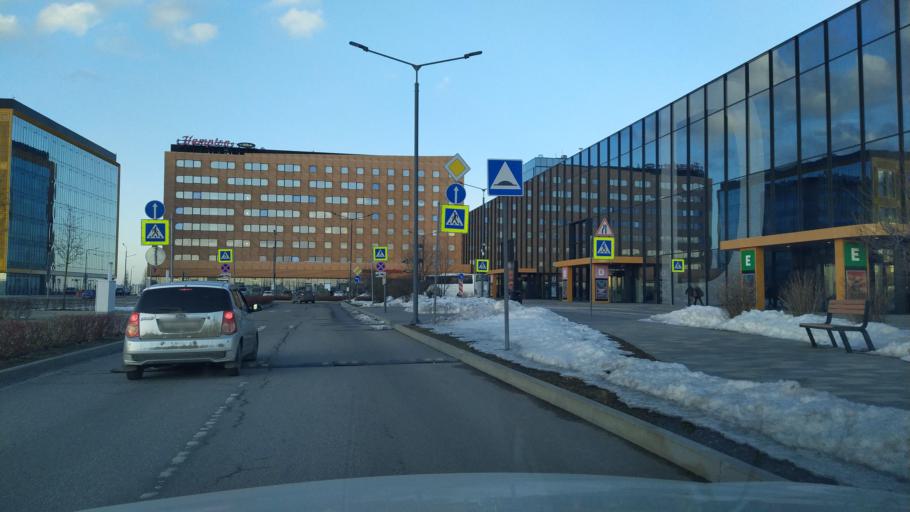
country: RU
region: St.-Petersburg
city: Aleksandrovskaya
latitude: 59.7624
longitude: 30.3545
